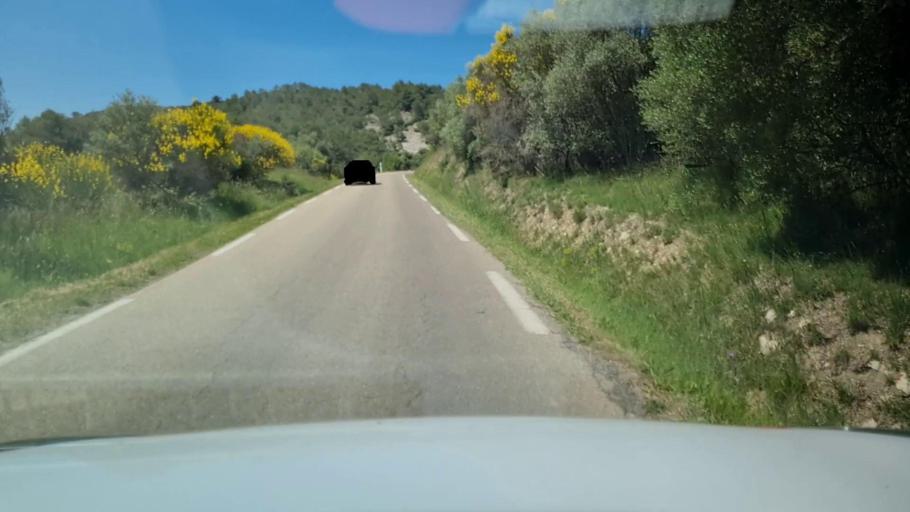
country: FR
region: Languedoc-Roussillon
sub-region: Departement du Gard
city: Clarensac
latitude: 43.8347
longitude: 4.2171
